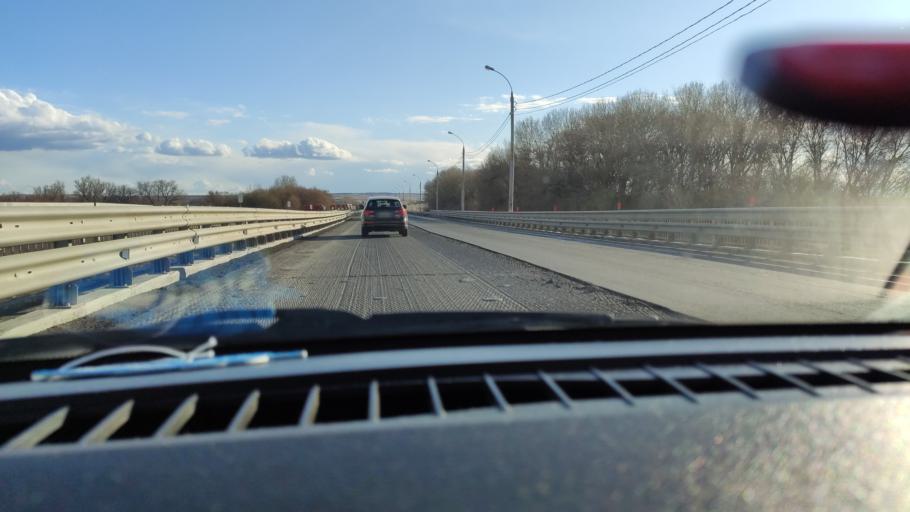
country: RU
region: Saratov
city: Yelshanka
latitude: 51.8227
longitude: 46.2180
